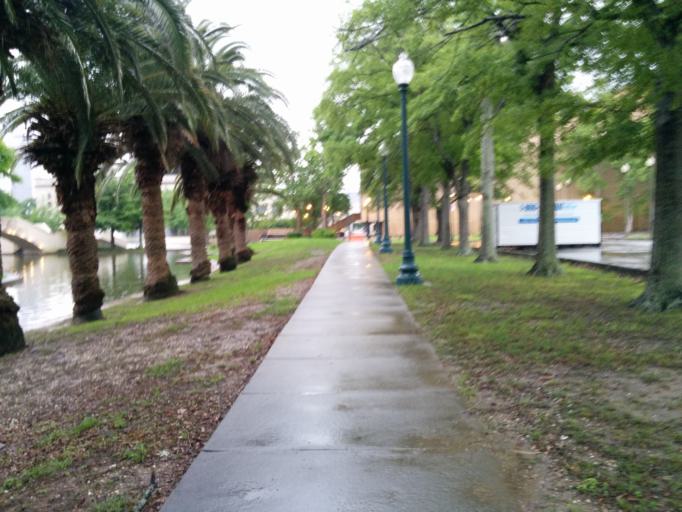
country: US
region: Louisiana
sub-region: Orleans Parish
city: New Orleans
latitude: 29.9638
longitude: -90.0684
